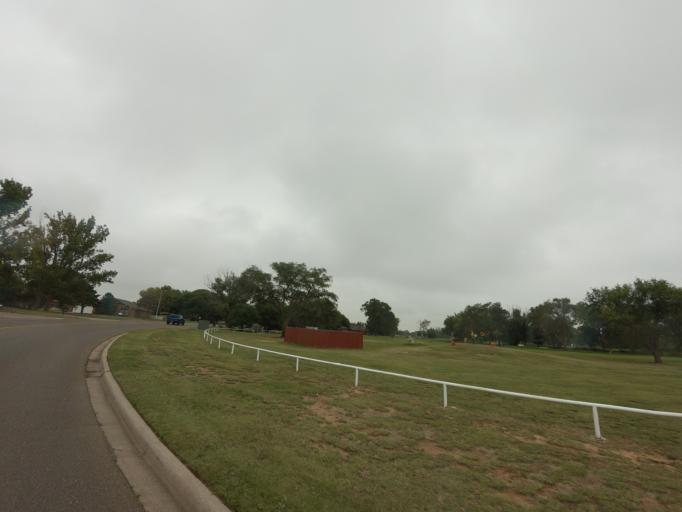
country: US
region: New Mexico
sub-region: Curry County
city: Clovis
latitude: 34.4407
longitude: -103.1931
